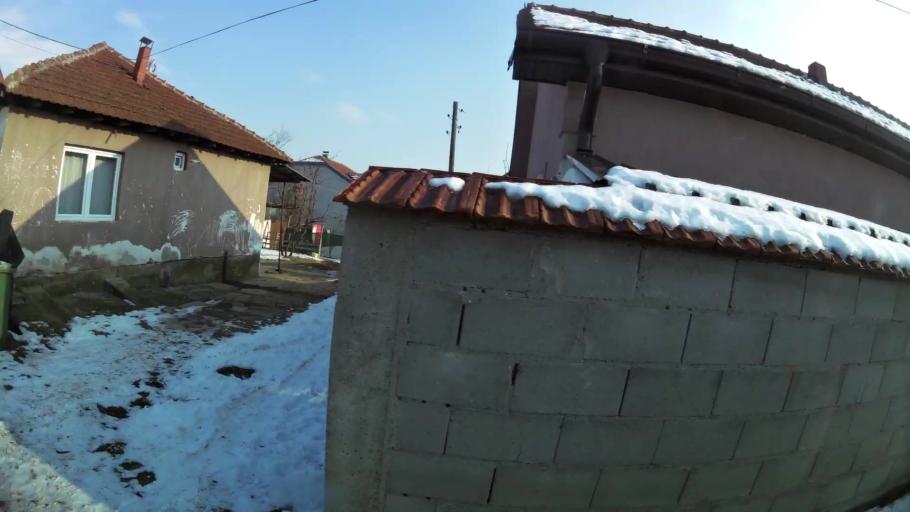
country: MK
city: Creshevo
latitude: 42.0223
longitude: 21.4981
